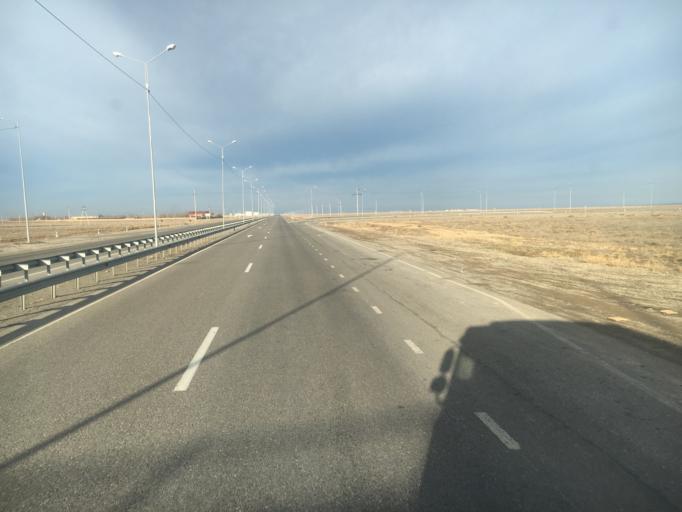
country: KZ
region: Ongtustik Qazaqstan
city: Turkestan
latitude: 43.4148
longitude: 68.0251
